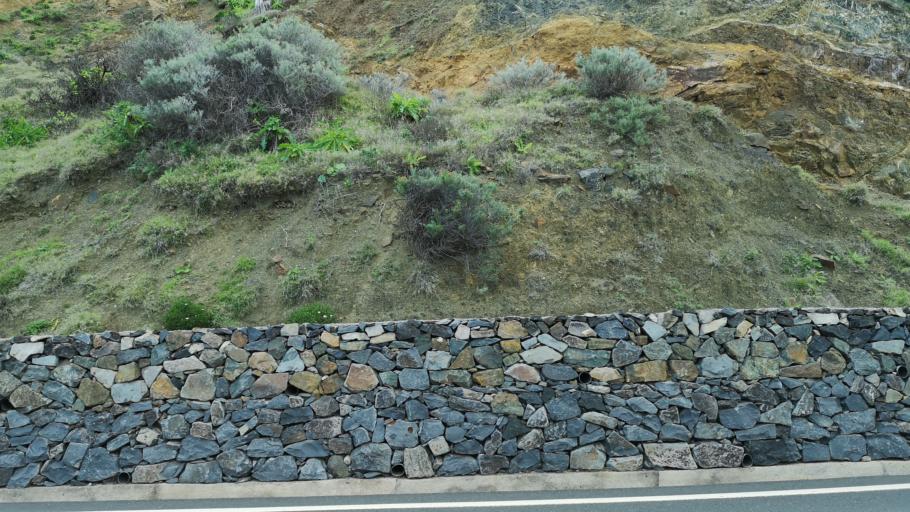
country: ES
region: Canary Islands
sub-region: Provincia de Santa Cruz de Tenerife
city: Agulo
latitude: 28.1905
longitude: -17.2049
